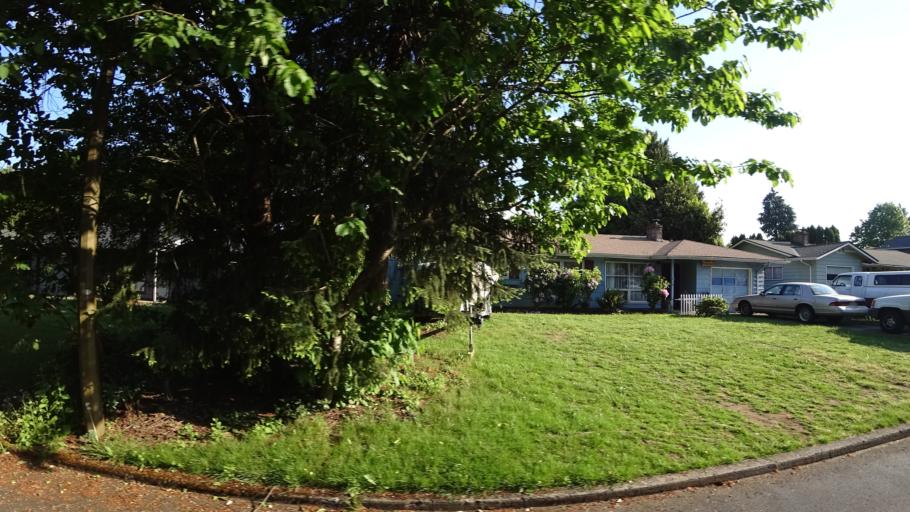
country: US
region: Oregon
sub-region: Multnomah County
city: Gresham
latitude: 45.5105
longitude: -122.4936
